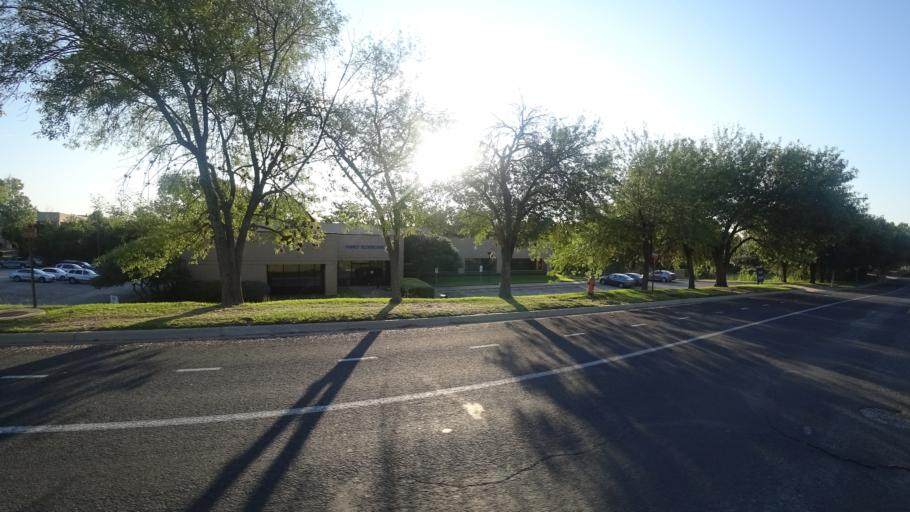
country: US
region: Texas
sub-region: Travis County
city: Austin
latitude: 30.3343
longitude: -97.6803
